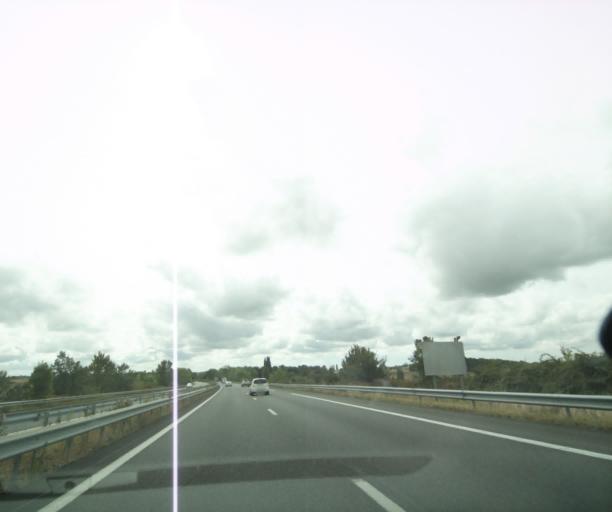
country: FR
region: Poitou-Charentes
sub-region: Departement de la Charente-Maritime
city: Mirambeau
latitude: 45.3850
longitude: -0.6033
